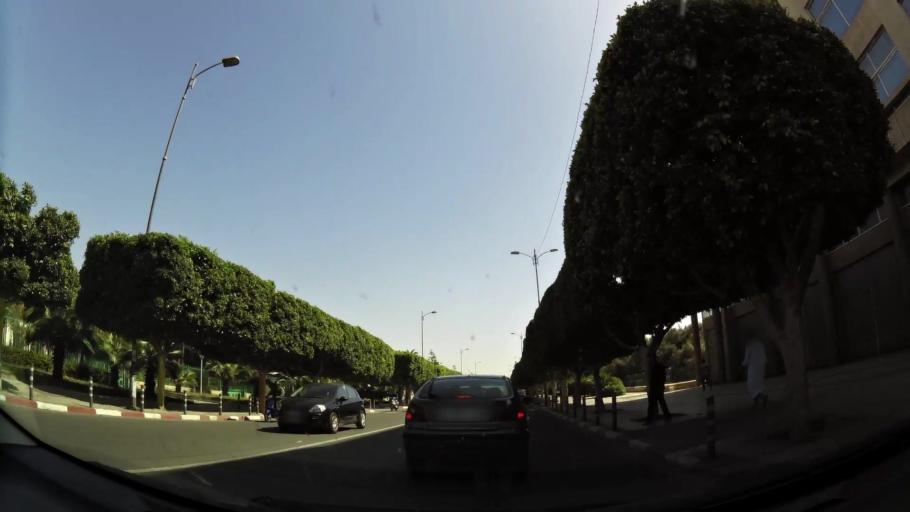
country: MA
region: Souss-Massa-Draa
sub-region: Inezgane-Ait Mellou
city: Inezgane
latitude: 30.3619
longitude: -9.5335
